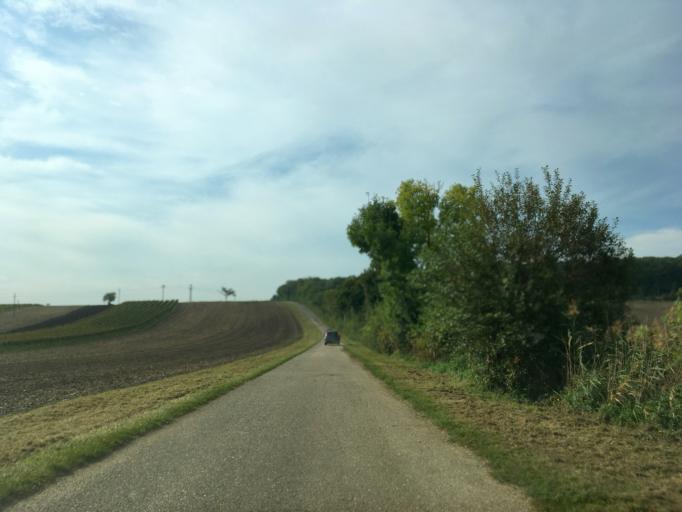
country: AT
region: Burgenland
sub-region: Politischer Bezirk Neusiedl am See
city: Jois
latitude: 47.9727
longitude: 16.8153
